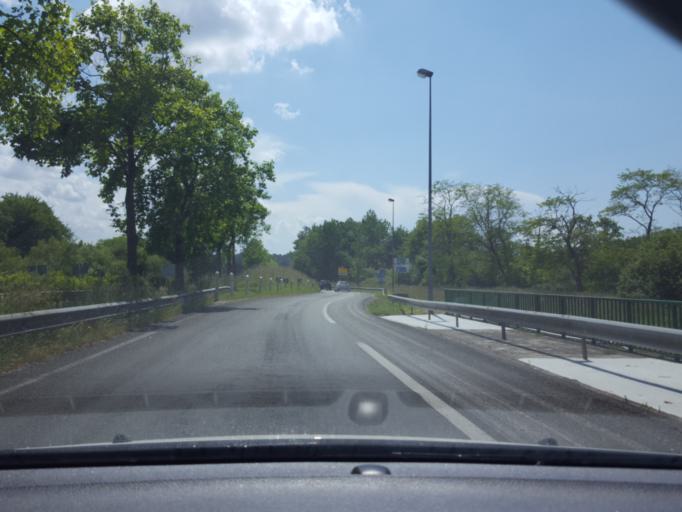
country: FR
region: Aquitaine
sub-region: Departement des Landes
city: Ondres
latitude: 43.5553
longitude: -1.4555
